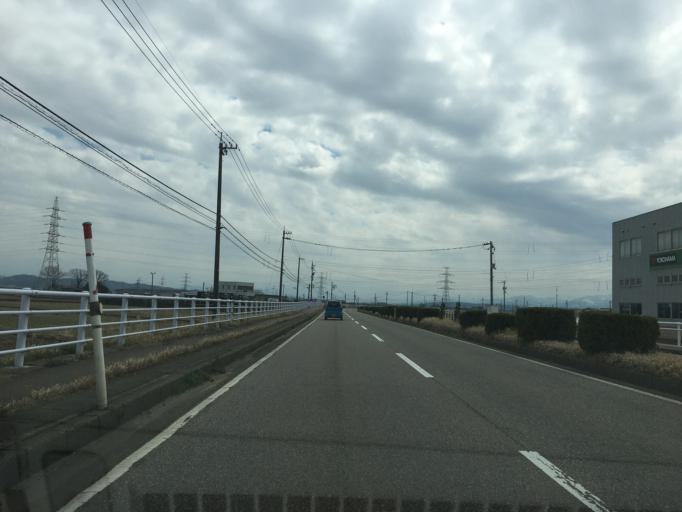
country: JP
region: Toyama
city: Kuragaki-kosugi
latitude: 36.7411
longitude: 137.1299
